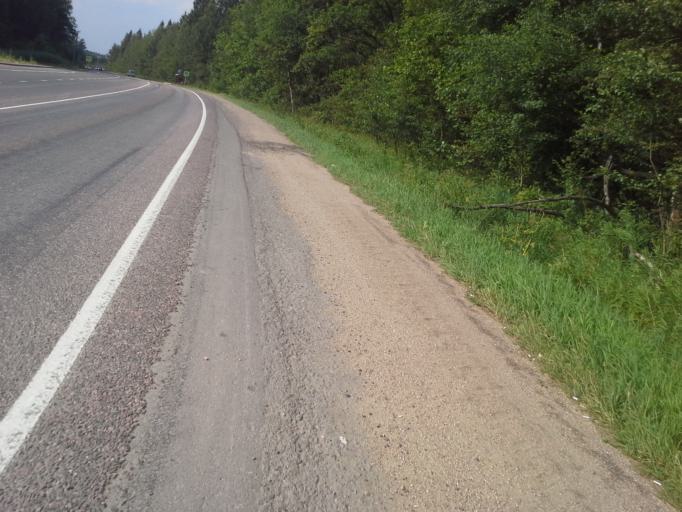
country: RU
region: Moskovskaya
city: Istra
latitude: 55.8673
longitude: 36.7992
